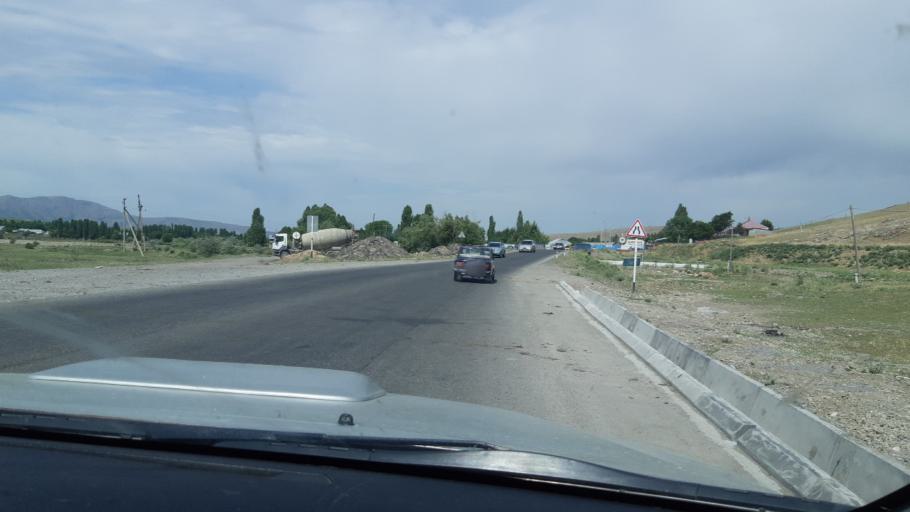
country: KZ
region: Ongtustik Qazaqstan
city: Turar Ryskulov
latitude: 42.5495
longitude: 70.3020
